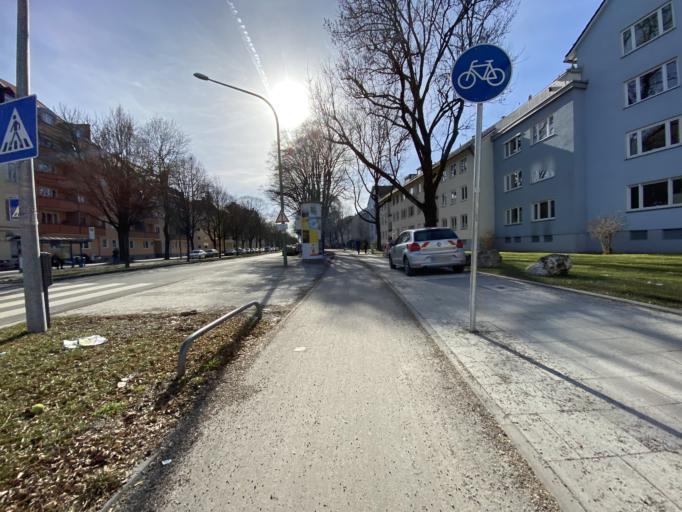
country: DE
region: Bavaria
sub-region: Upper Bavaria
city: Munich
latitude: 48.1104
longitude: 11.5671
